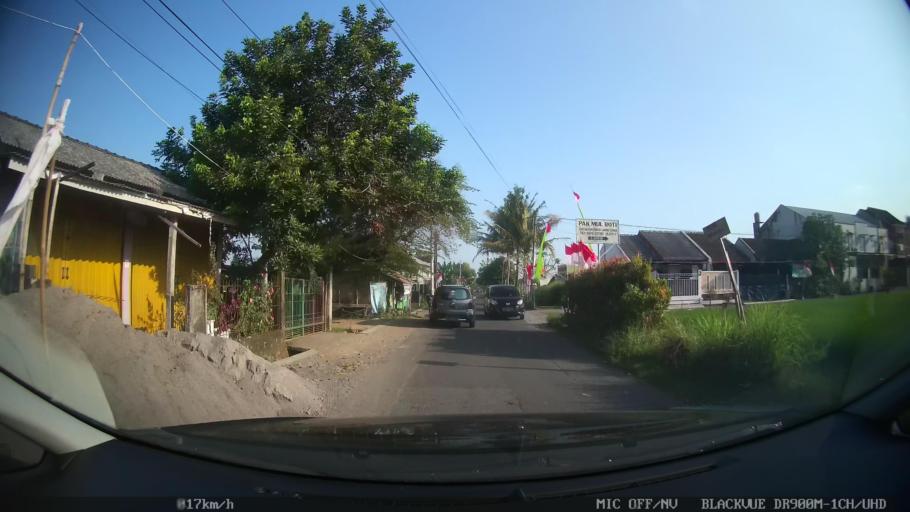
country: ID
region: Daerah Istimewa Yogyakarta
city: Gamping Lor
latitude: -7.7909
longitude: 110.3335
